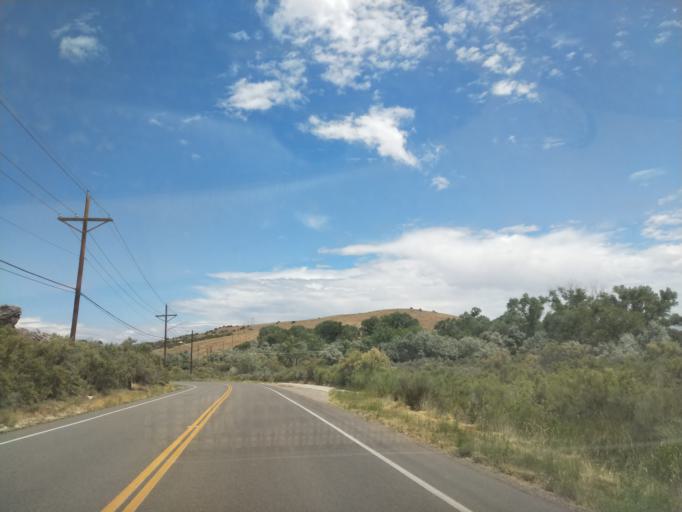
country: US
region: Colorado
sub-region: Mesa County
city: Redlands
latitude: 39.0726
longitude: -108.6443
